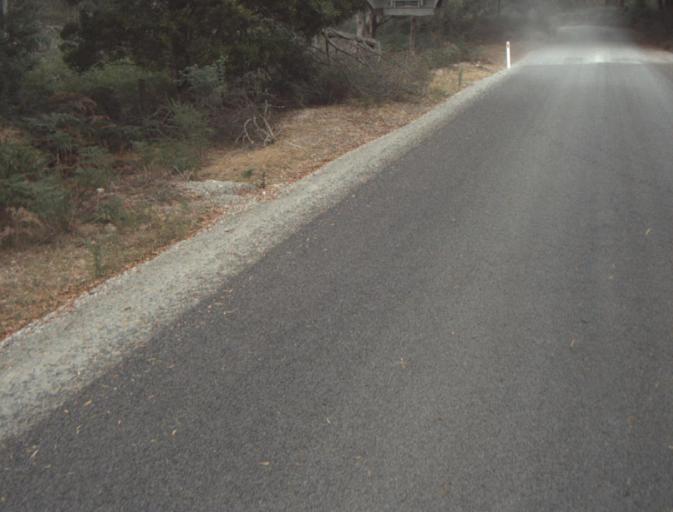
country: AU
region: Tasmania
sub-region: Launceston
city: Mayfield
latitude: -41.1921
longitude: 147.1615
